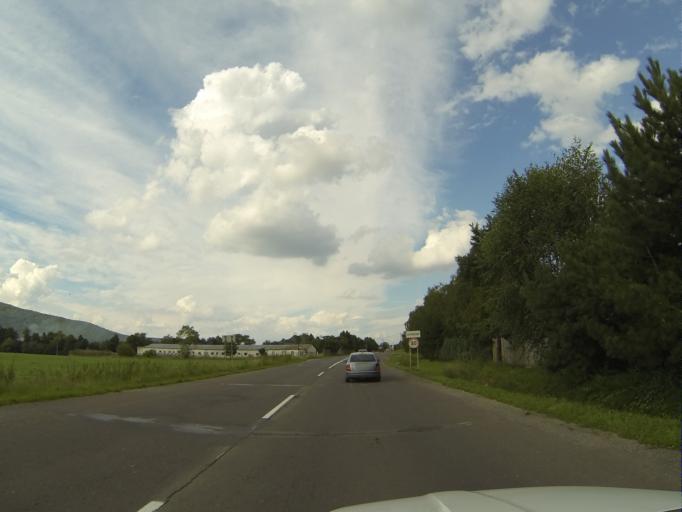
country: SK
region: Nitriansky
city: Novaky
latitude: 48.6584
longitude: 18.5078
